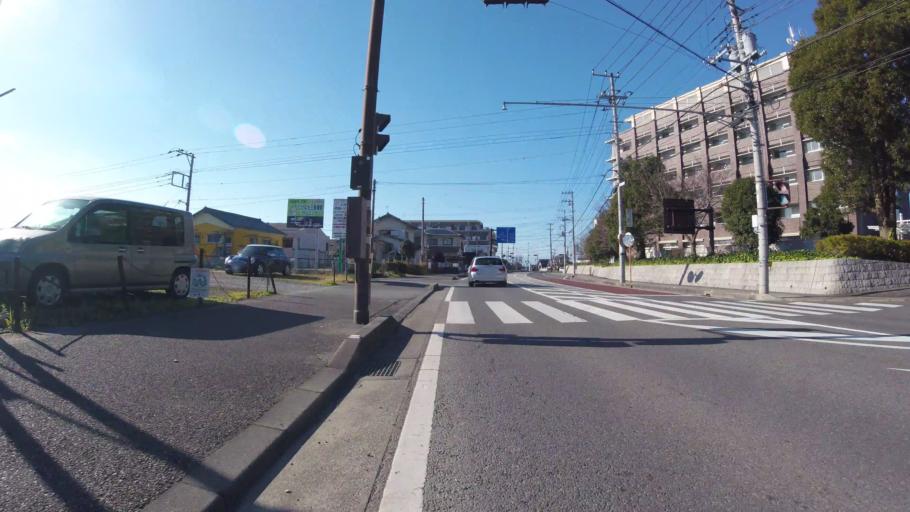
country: JP
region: Shizuoka
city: Mishima
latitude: 35.0883
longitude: 138.9540
